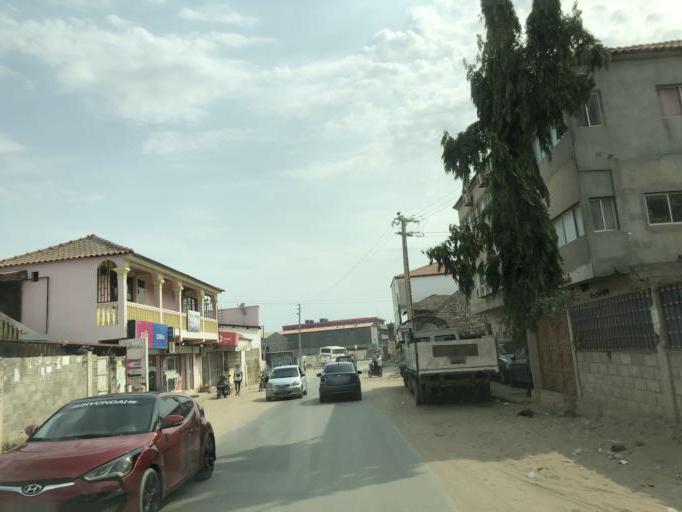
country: AO
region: Luanda
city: Luanda
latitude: -8.9016
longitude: 13.3482
